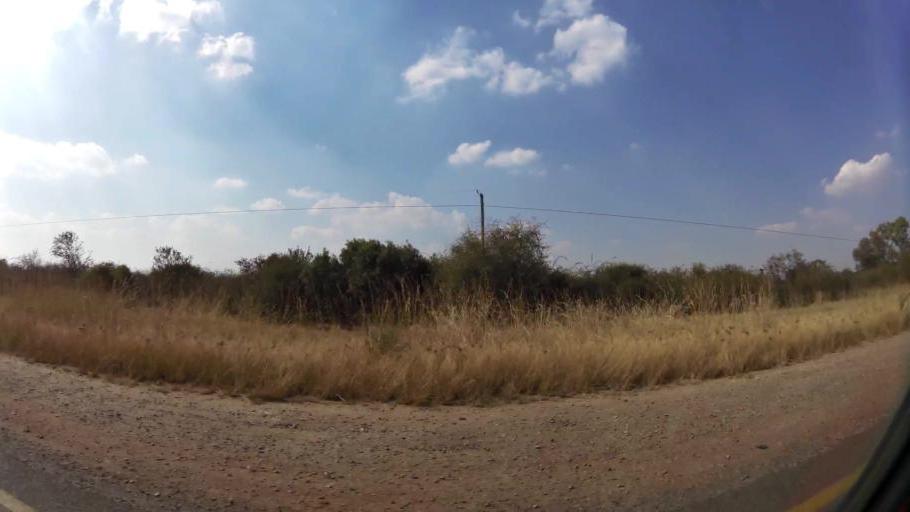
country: ZA
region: North-West
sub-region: Bojanala Platinum District Municipality
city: Rustenburg
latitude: -25.5412
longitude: 27.1236
